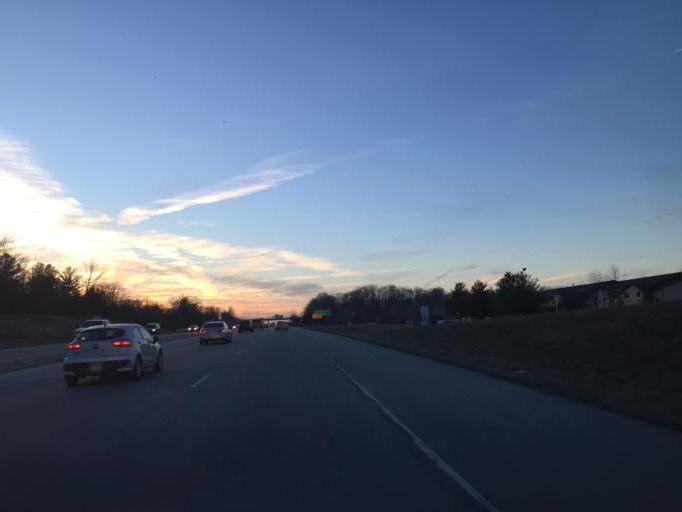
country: US
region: Indiana
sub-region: Monroe County
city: Bloomington
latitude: 39.1868
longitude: -86.5435
